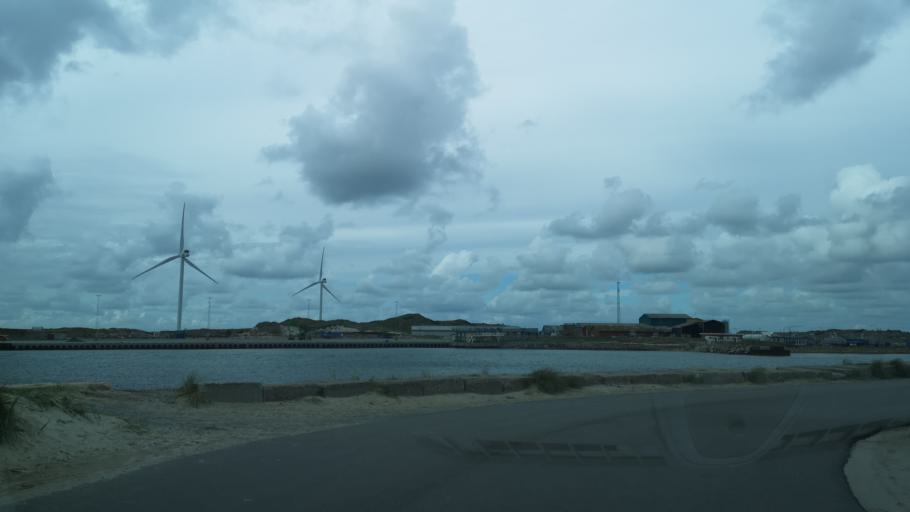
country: DK
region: Central Jutland
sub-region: Ringkobing-Skjern Kommune
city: Hvide Sande
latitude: 55.9994
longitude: 8.1212
